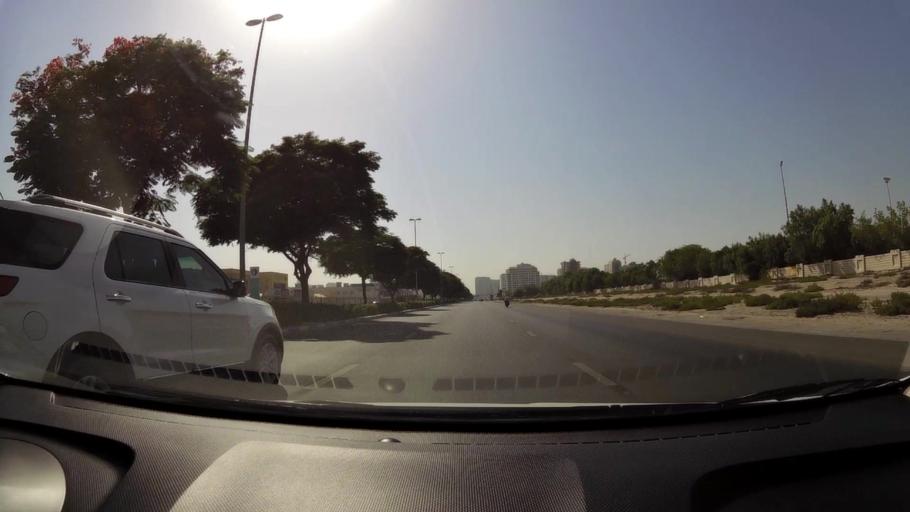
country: AE
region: Ash Shariqah
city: Sharjah
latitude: 25.2826
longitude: 55.3764
